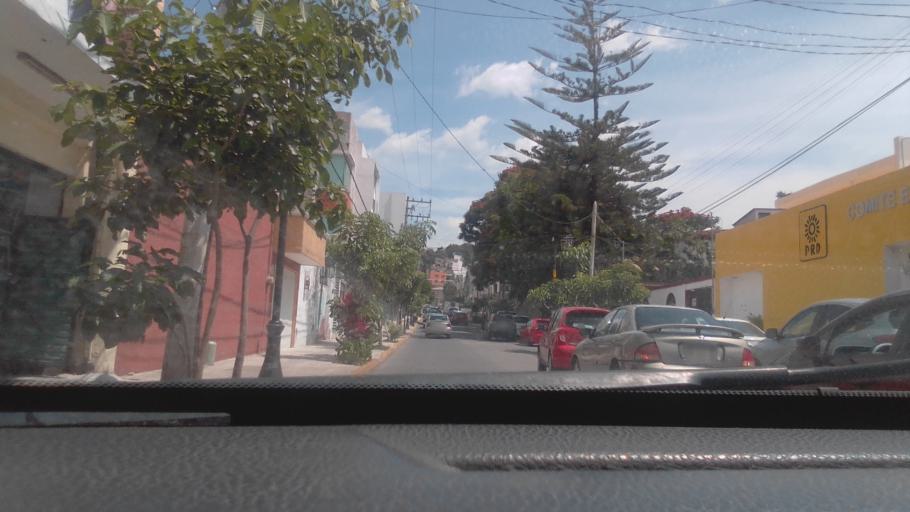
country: MX
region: Guerrero
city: Chilpancingo de los Bravos
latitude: 17.5463
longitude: -99.4979
